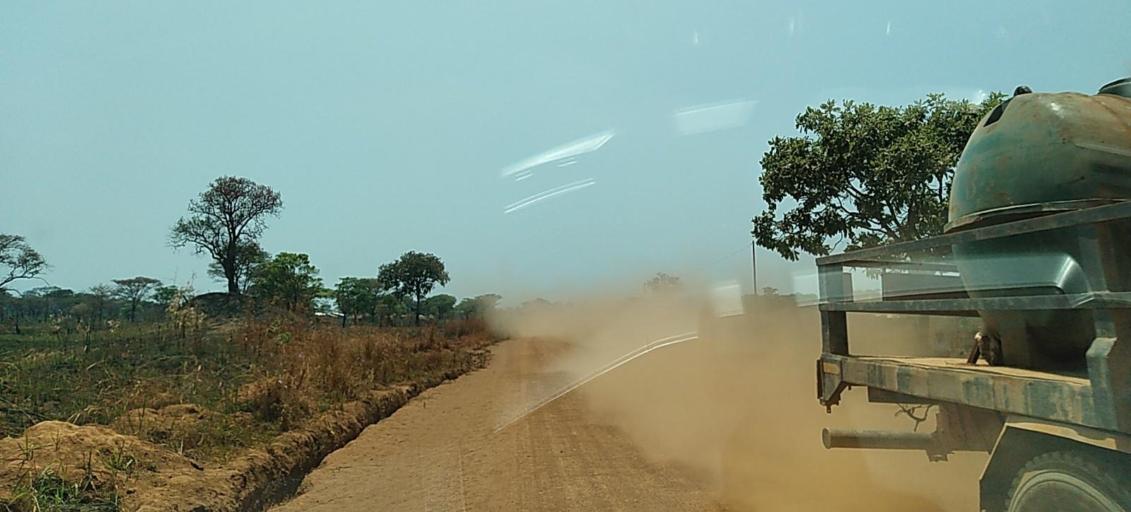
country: CD
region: Katanga
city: Kipushi
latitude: -11.9361
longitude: 26.9603
